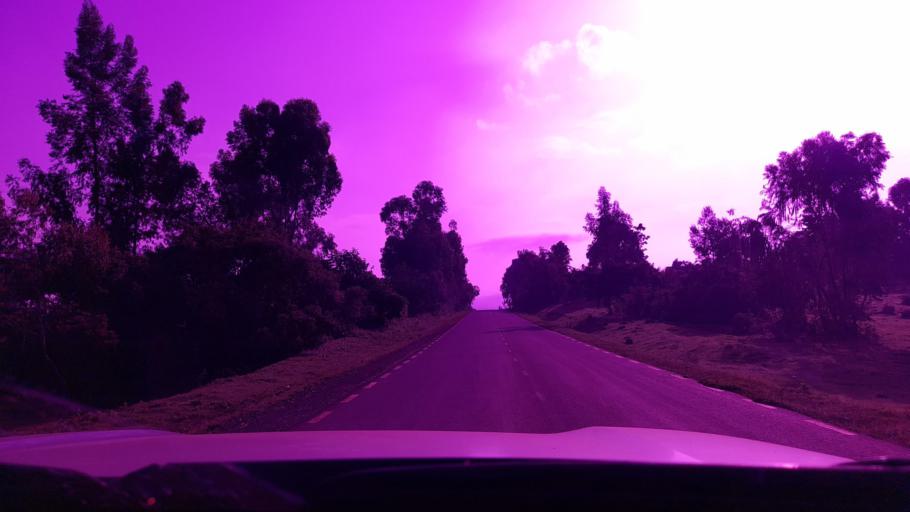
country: ET
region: Oromiya
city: Bedele
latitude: 8.1524
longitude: 36.4681
